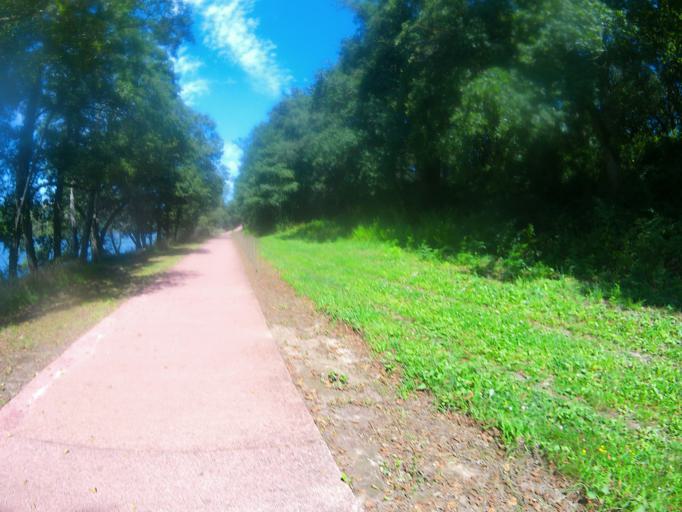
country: PT
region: Viana do Castelo
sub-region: Valenca
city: Valenca
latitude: 41.9942
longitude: -8.6732
